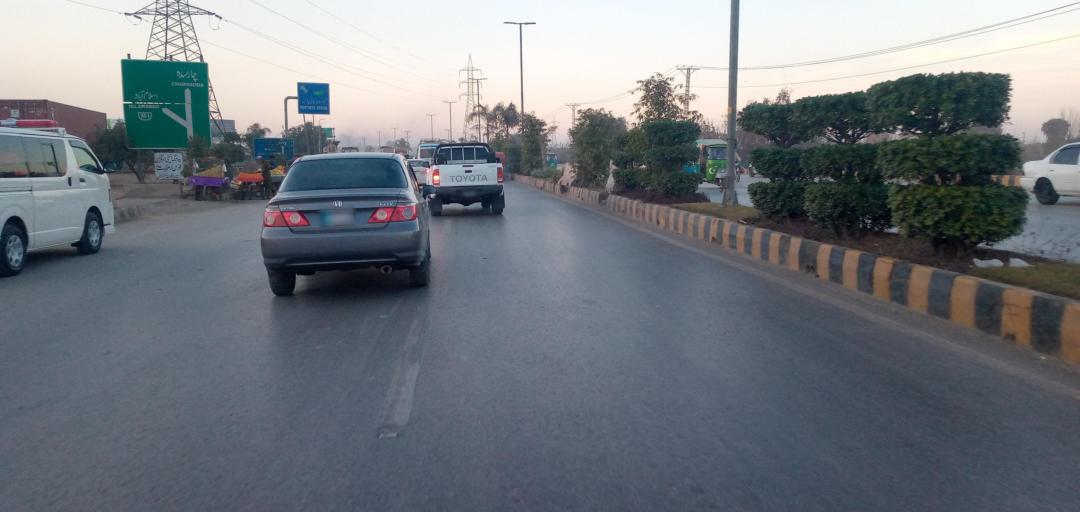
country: PK
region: Khyber Pakhtunkhwa
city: Peshawar
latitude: 34.0248
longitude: 71.6196
